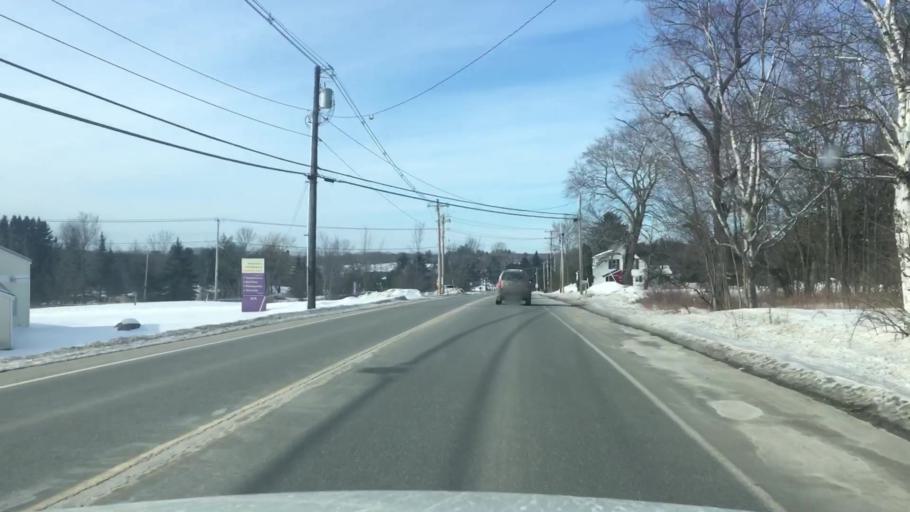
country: US
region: Maine
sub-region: Penobscot County
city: Bangor
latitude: 44.8487
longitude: -68.8034
